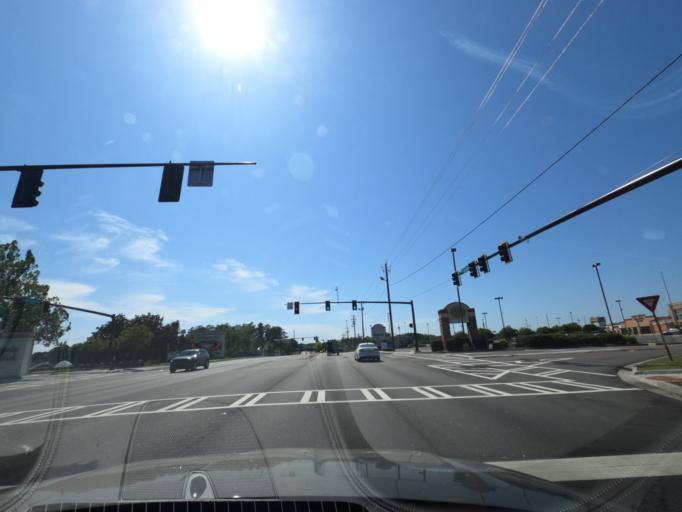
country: US
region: Georgia
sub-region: Columbia County
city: Martinez
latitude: 33.4677
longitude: -82.0799
